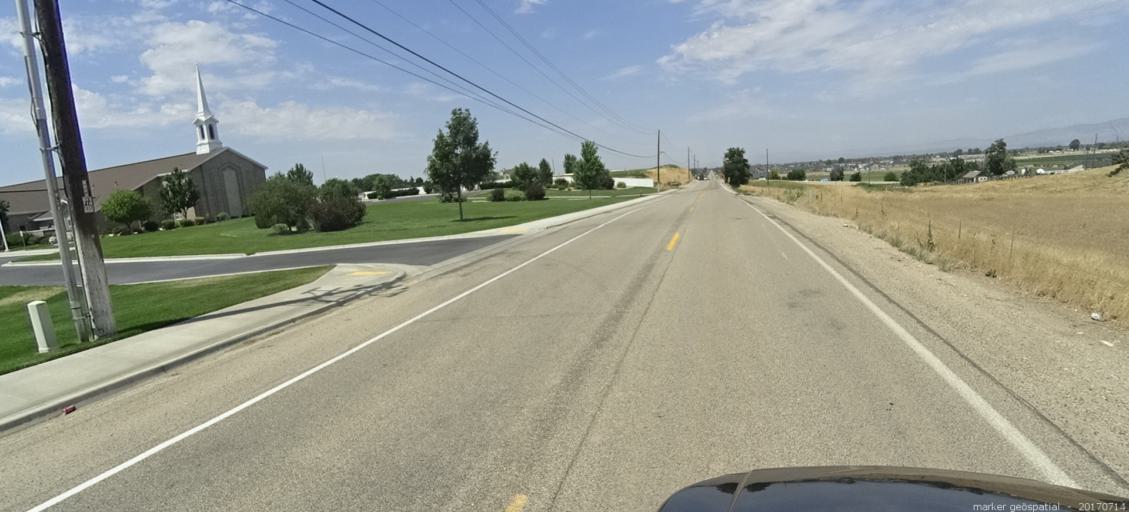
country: US
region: Idaho
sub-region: Ada County
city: Meridian
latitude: 43.5437
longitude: -116.3543
